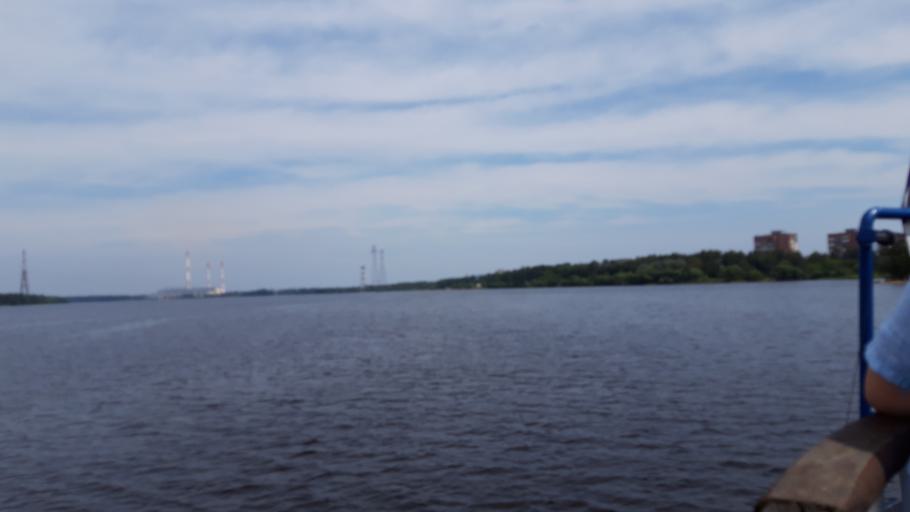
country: RU
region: Tverskaya
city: Konakovo
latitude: 56.7075
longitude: 36.7494
